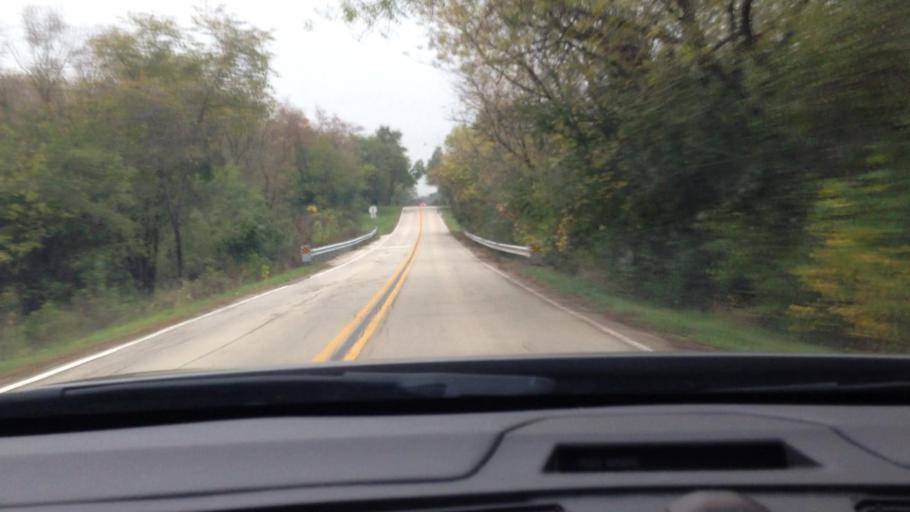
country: US
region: Illinois
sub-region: Cook County
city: Streamwood
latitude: 42.0897
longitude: -88.1946
